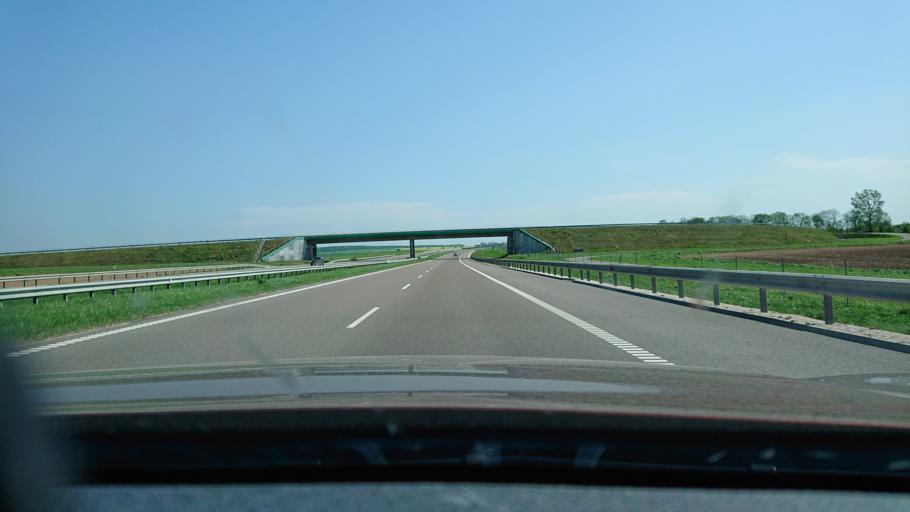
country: PL
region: Subcarpathian Voivodeship
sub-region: Powiat przemyski
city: Stubno
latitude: 49.9356
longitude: 22.9357
